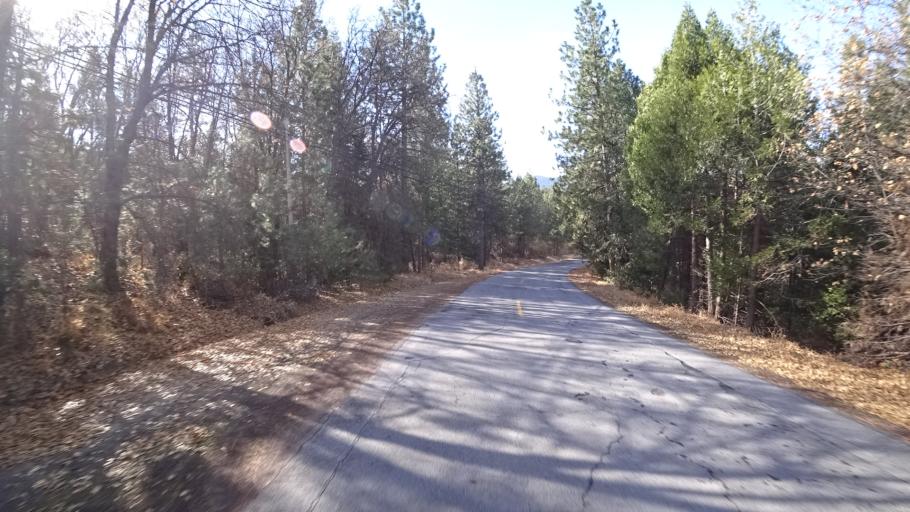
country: US
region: California
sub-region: Siskiyou County
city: Weed
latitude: 41.4298
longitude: -122.4184
